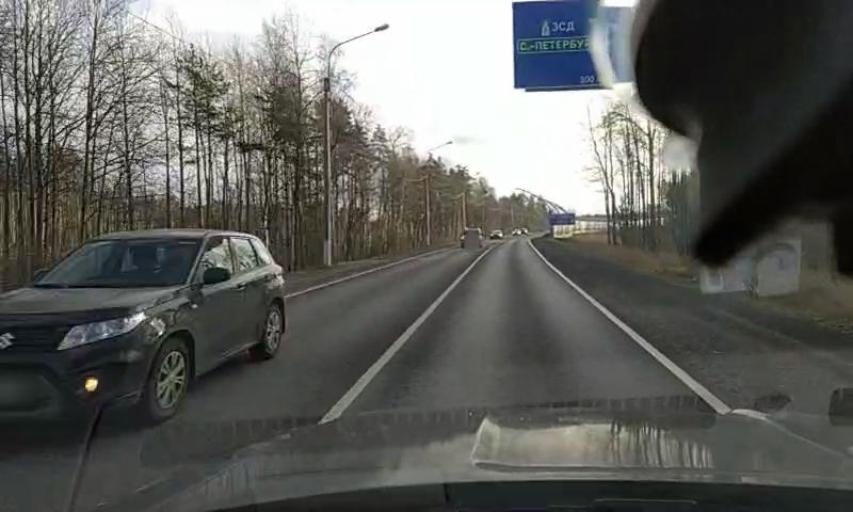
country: RU
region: St.-Petersburg
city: Solnechnoye
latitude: 60.1539
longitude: 29.9639
